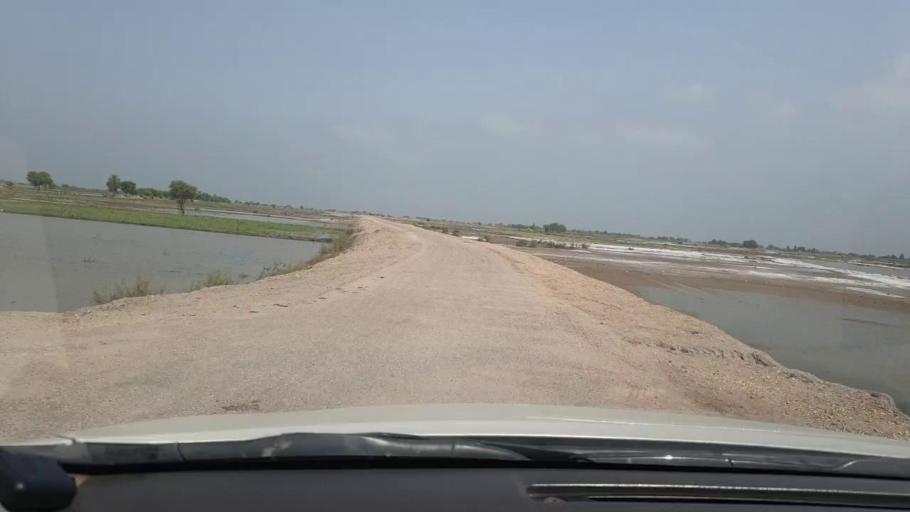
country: PK
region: Sindh
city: Shikarpur
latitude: 27.9935
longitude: 68.5630
